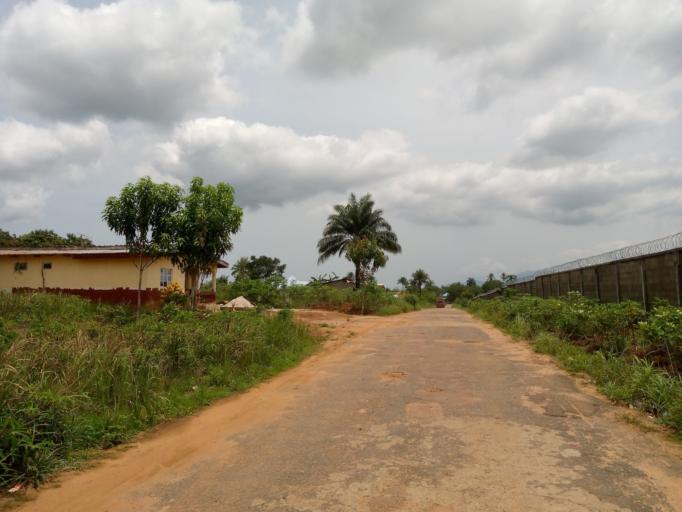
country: SL
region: Western Area
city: Waterloo
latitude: 8.3517
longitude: -12.9802
